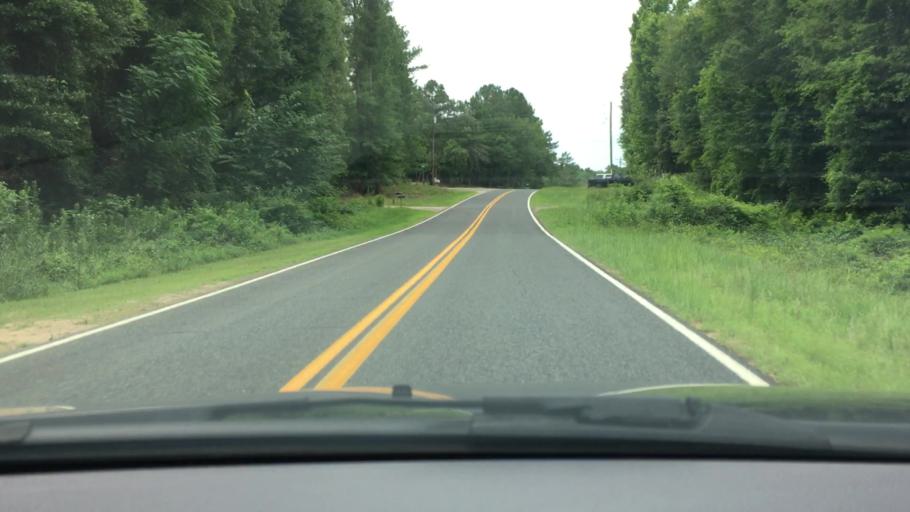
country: US
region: South Carolina
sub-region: Barnwell County
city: Williston
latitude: 33.6231
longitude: -81.3726
